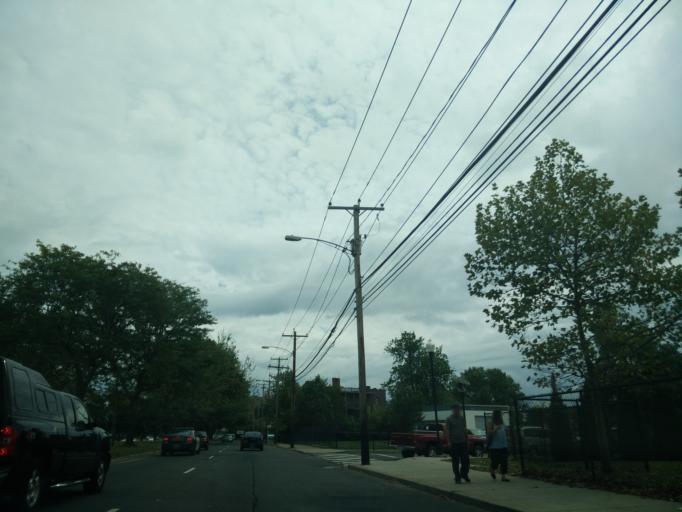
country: US
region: Connecticut
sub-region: Fairfield County
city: Bridgeport
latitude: 41.1947
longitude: -73.1752
